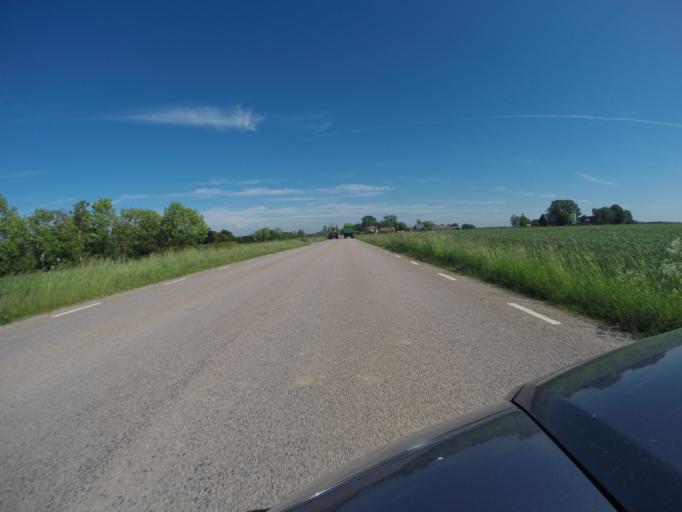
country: SE
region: Skane
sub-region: Helsingborg
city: Odakra
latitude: 56.1087
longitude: 12.7108
